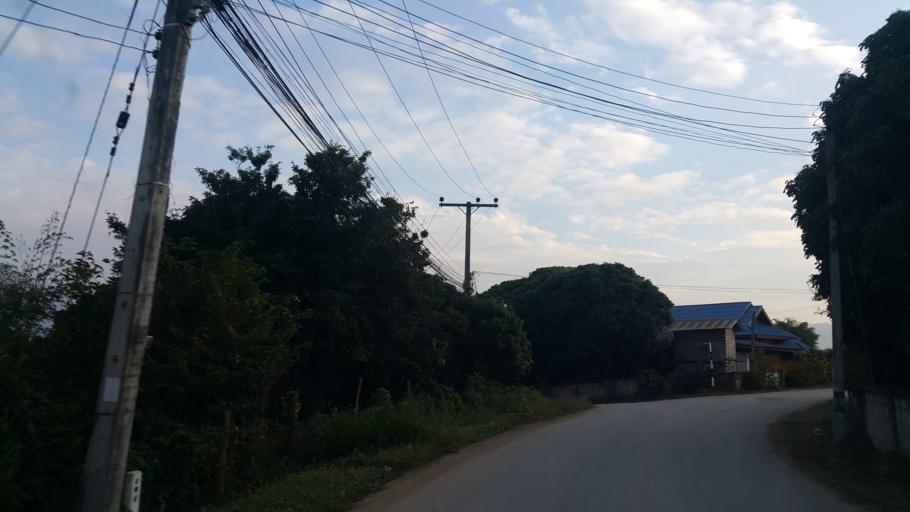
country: TH
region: Lampang
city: Sop Prap
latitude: 17.8984
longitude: 99.3307
